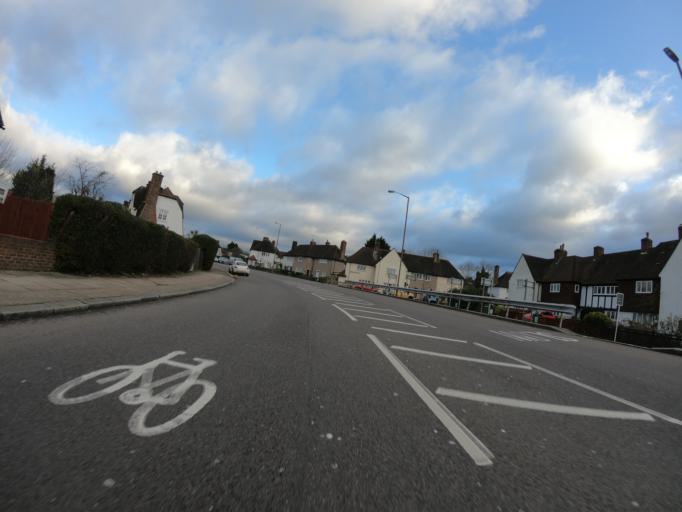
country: GB
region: England
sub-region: Greater London
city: Woolwich
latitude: 51.4608
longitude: 0.0529
